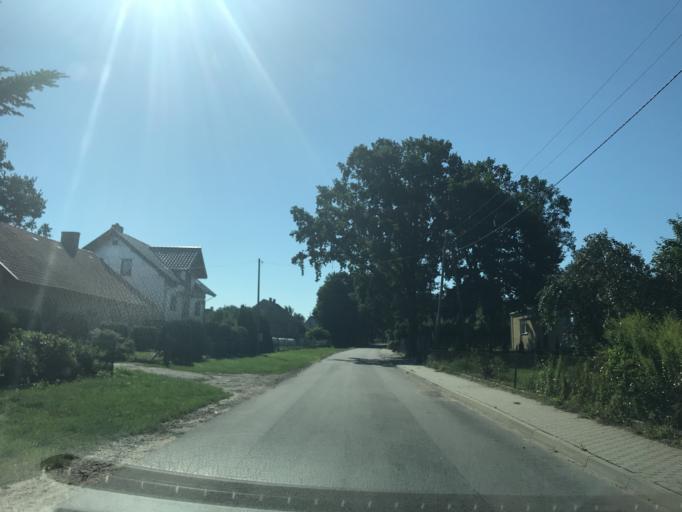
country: PL
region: Warmian-Masurian Voivodeship
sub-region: Powiat ostrodzki
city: Ostroda
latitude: 53.5945
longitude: 19.9041
